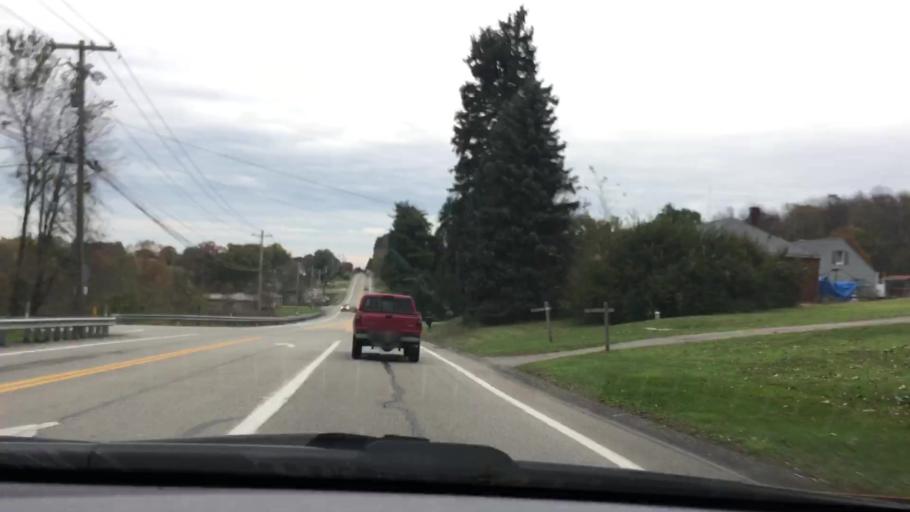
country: US
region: Pennsylvania
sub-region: Armstrong County
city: Apollo
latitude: 40.5413
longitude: -79.5917
